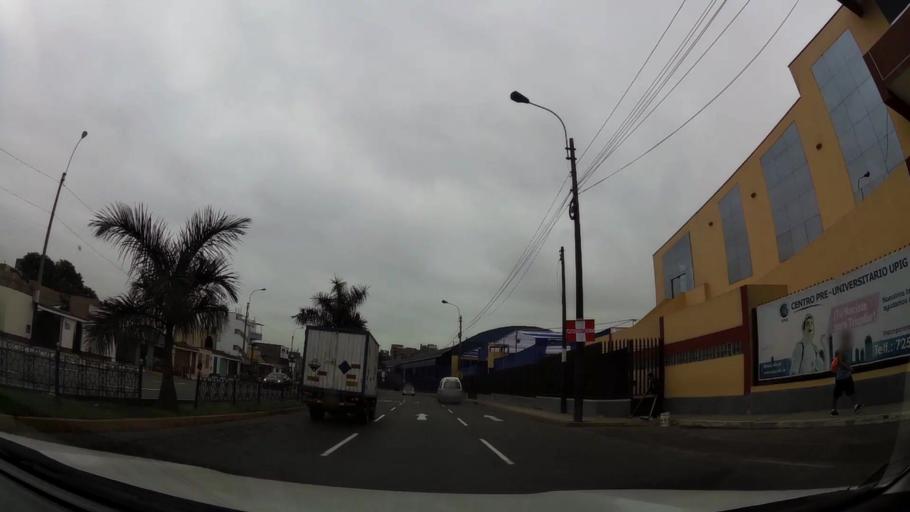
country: PE
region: Lima
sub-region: Lima
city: Surco
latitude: -12.1825
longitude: -77.0113
